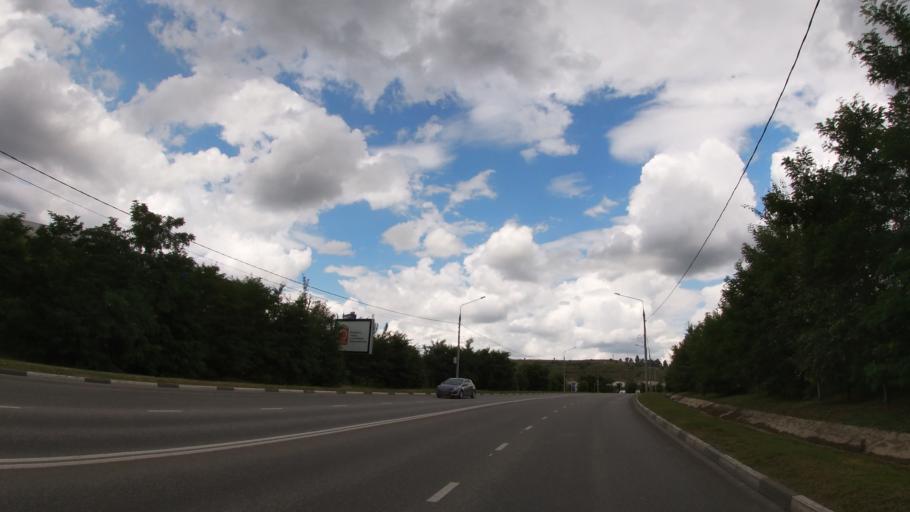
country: RU
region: Belgorod
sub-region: Belgorodskiy Rayon
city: Belgorod
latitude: 50.6111
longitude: 36.6125
